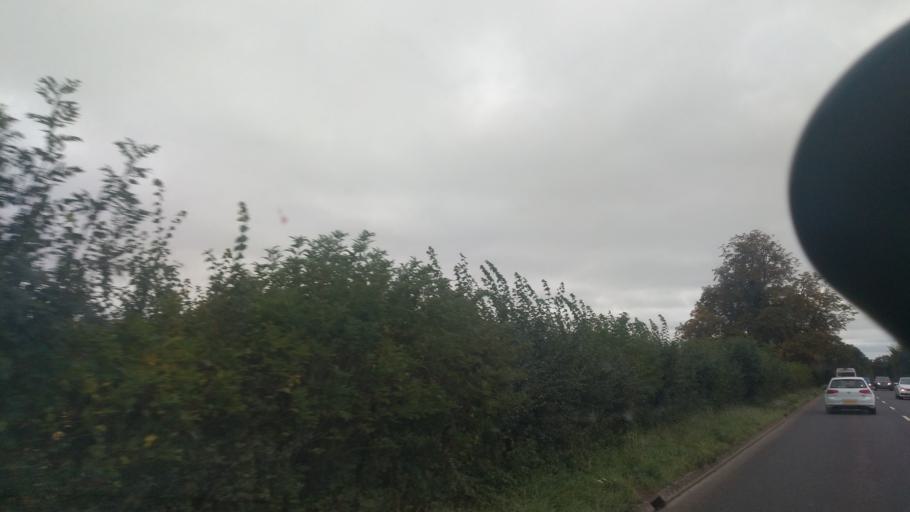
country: GB
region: England
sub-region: Wiltshire
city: Trowbridge
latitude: 51.3152
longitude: -2.1674
